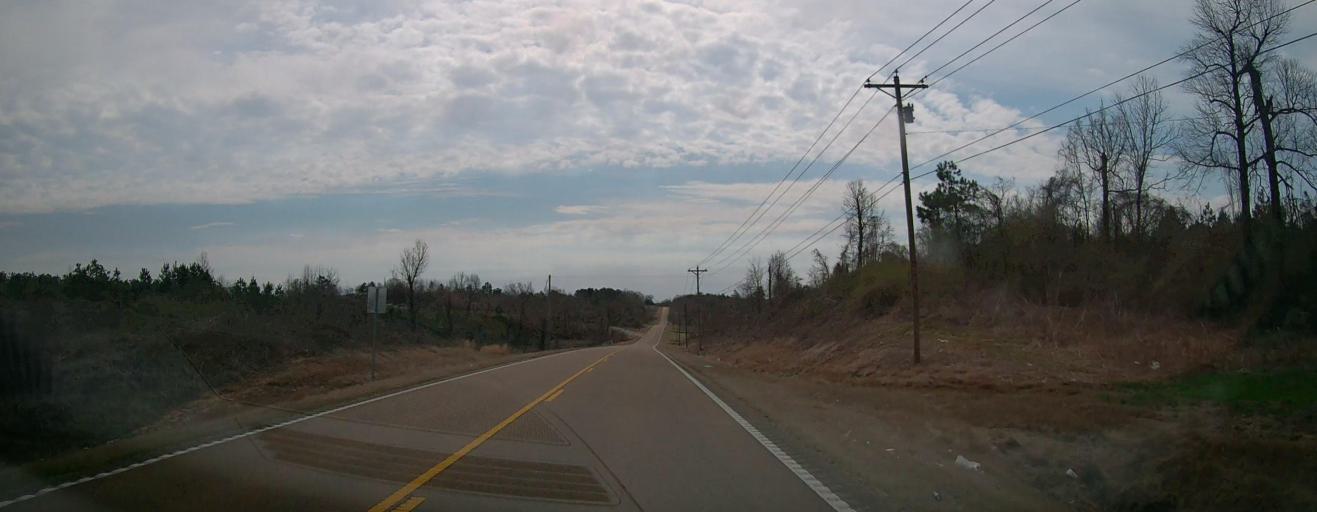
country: US
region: Mississippi
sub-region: Marshall County
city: Holly Springs
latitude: 34.7485
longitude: -89.4283
